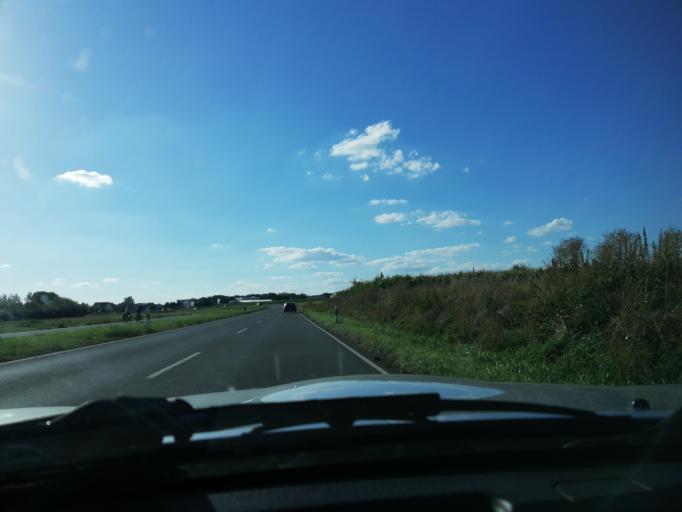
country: DE
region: Bavaria
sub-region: Regierungsbezirk Mittelfranken
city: Grossenseebach
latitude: 49.6323
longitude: 10.8875
